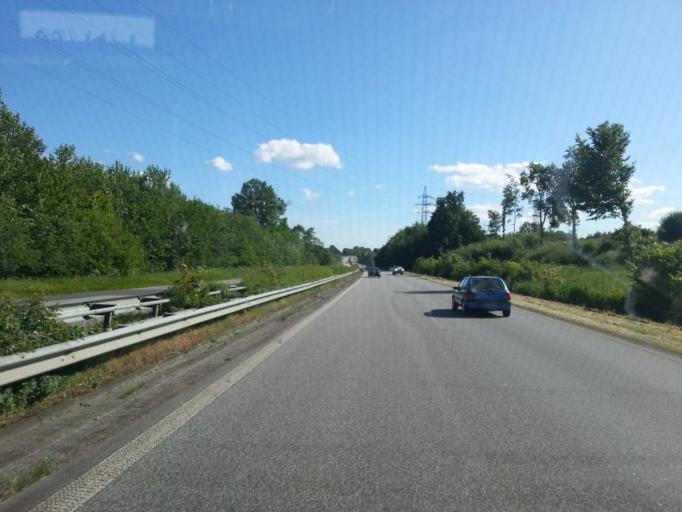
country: DE
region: Schleswig-Holstein
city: Neustadt in Holstein
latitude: 54.1109
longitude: 10.7832
